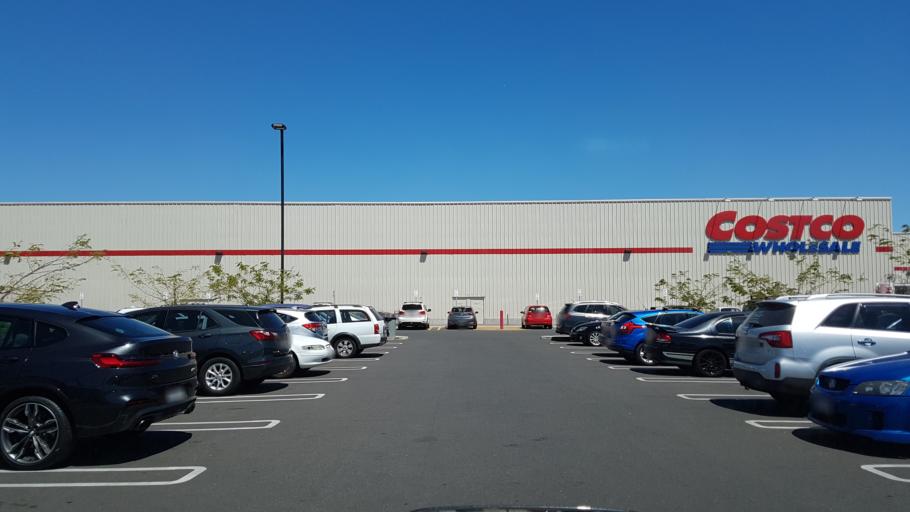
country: AU
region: South Australia
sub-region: Port Adelaide Enfield
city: Blair Athol
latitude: -34.8631
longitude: 138.5821
